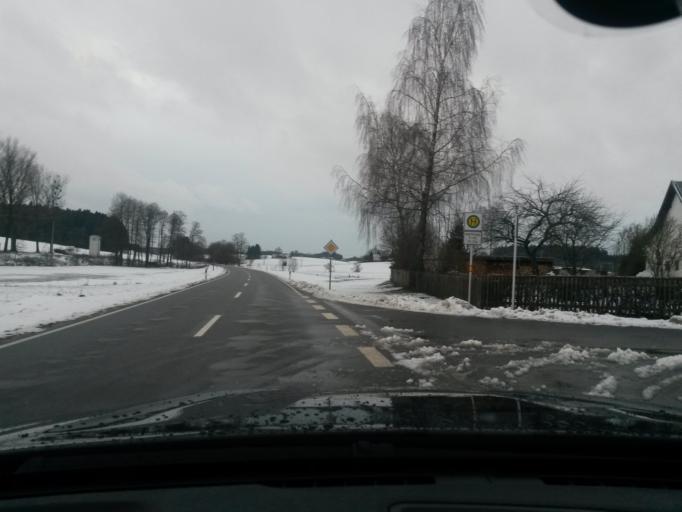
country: DE
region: Bavaria
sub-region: Lower Bavaria
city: Vilsheim
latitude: 48.4424
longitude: 12.0856
